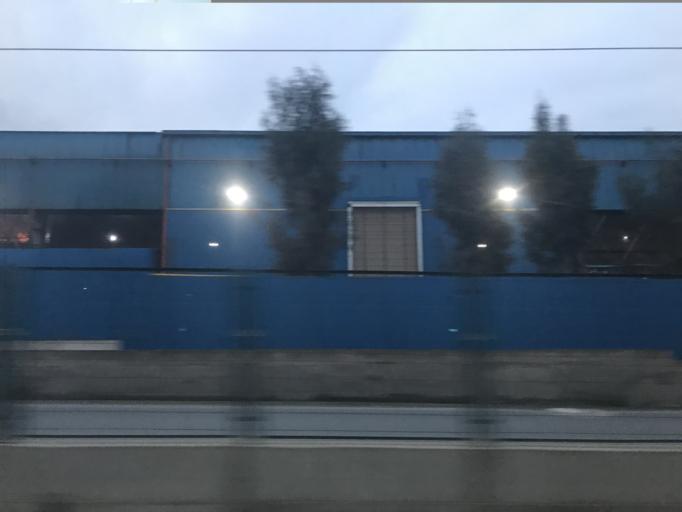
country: TR
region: Kocaeli
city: Darica
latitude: 40.8022
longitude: 29.3753
